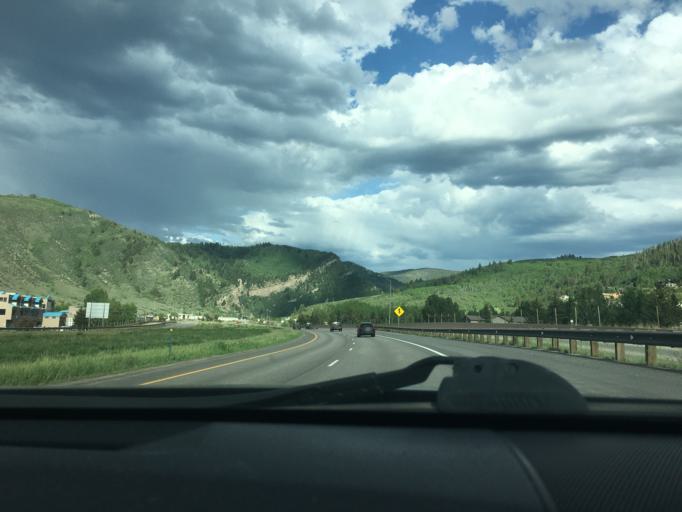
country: US
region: Colorado
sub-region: Eagle County
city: Avon
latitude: 39.6216
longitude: -106.4825
